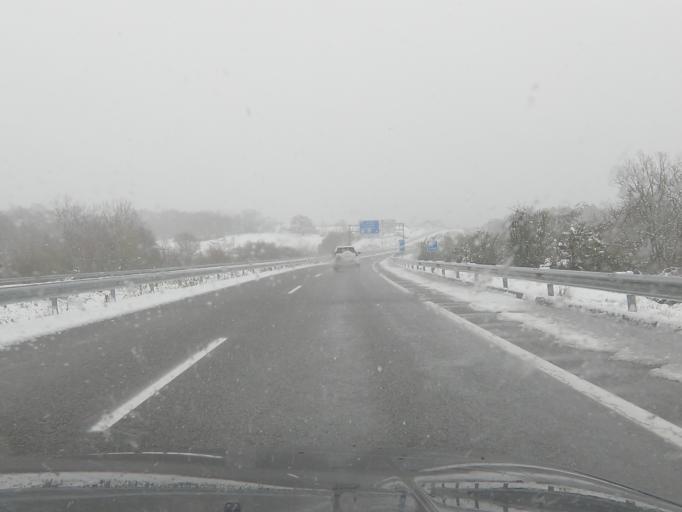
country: ES
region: Galicia
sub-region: Provincia de Ourense
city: Rios
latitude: 41.9812
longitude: -7.2944
